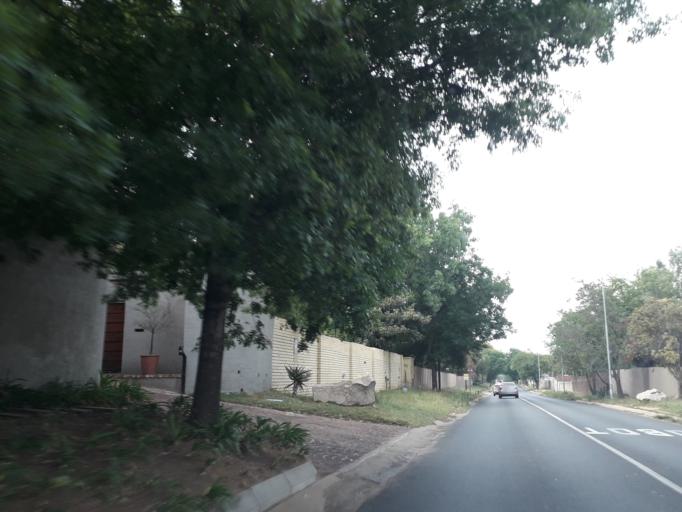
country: ZA
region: Gauteng
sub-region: City of Johannesburg Metropolitan Municipality
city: Midrand
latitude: -26.0760
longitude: 28.0457
